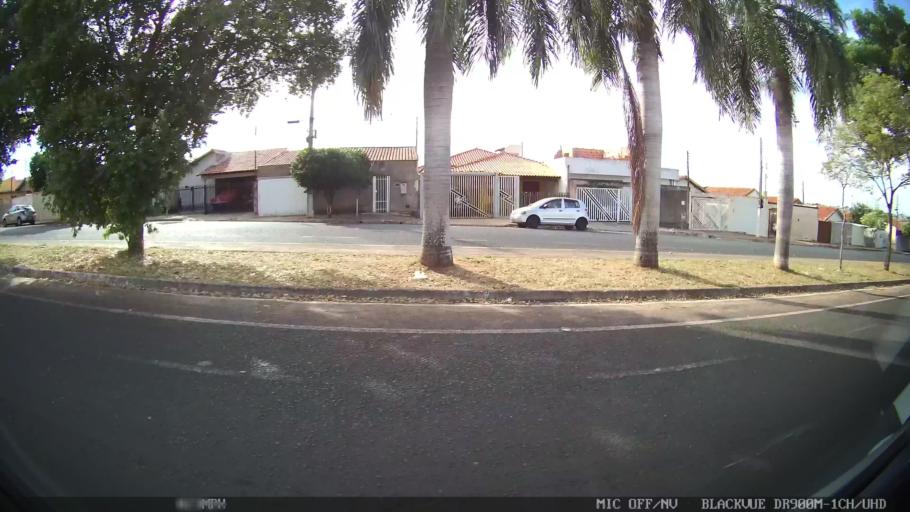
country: BR
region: Sao Paulo
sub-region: Catanduva
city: Catanduva
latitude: -21.1306
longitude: -48.9956
